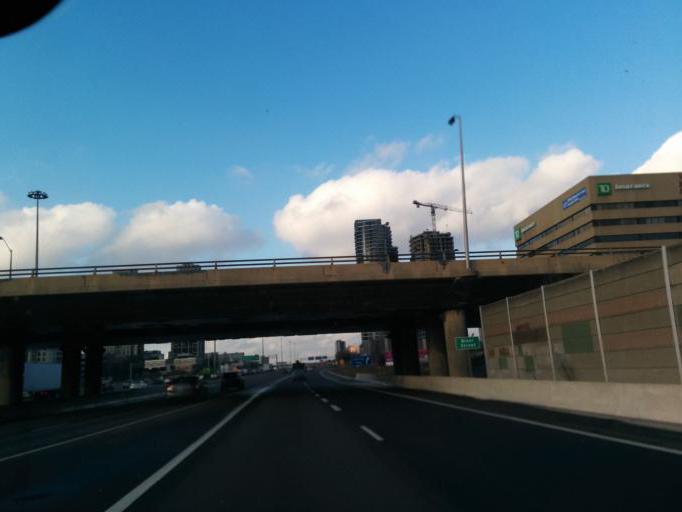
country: CA
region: Ontario
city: Etobicoke
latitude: 43.6359
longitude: -79.5589
